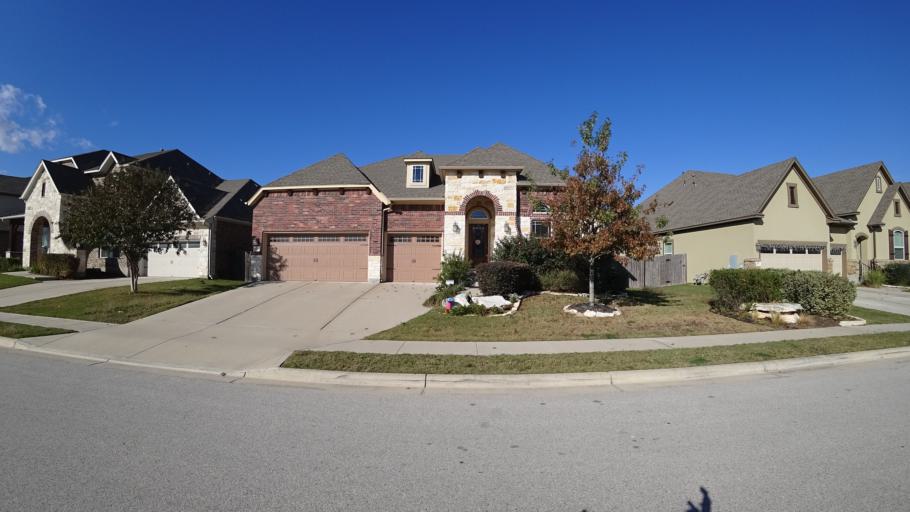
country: US
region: Texas
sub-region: Williamson County
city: Brushy Creek
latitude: 30.4868
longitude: -97.7253
